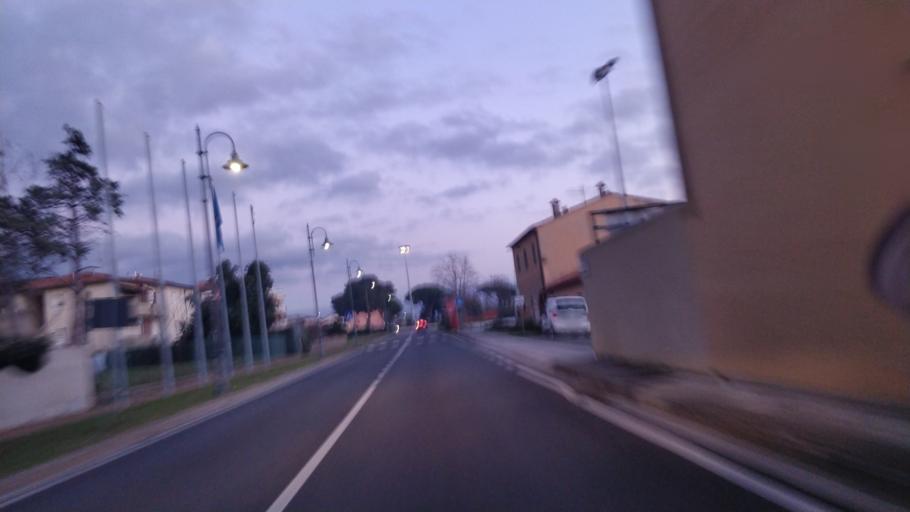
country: IT
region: Tuscany
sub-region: Provincia di Livorno
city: Vada
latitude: 43.3499
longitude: 10.4608
